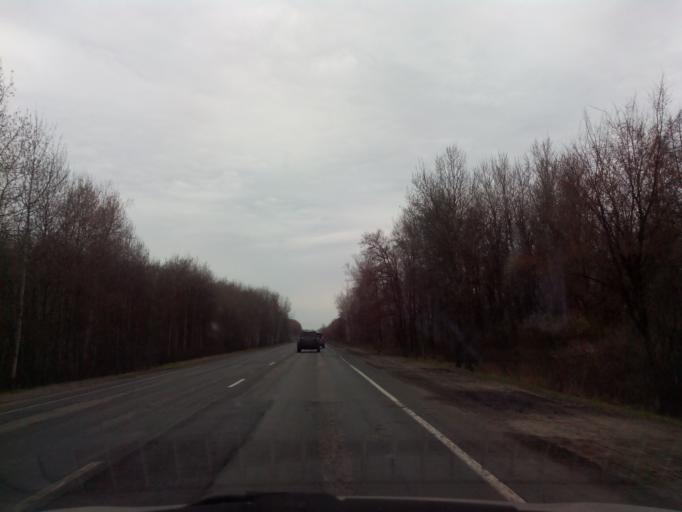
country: RU
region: Tambov
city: Zavoronezhskoye
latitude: 52.9376
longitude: 40.6029
